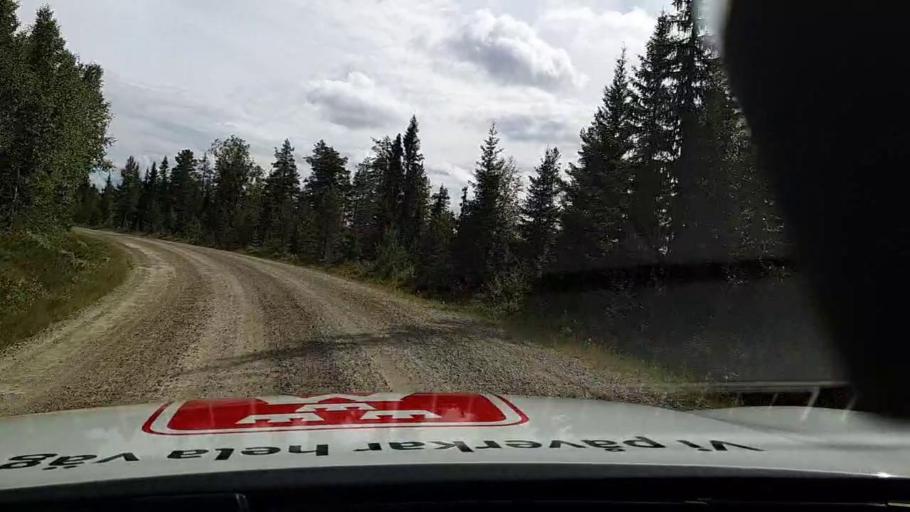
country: SE
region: Jaemtland
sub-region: Are Kommun
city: Jarpen
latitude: 62.5408
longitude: 13.4727
